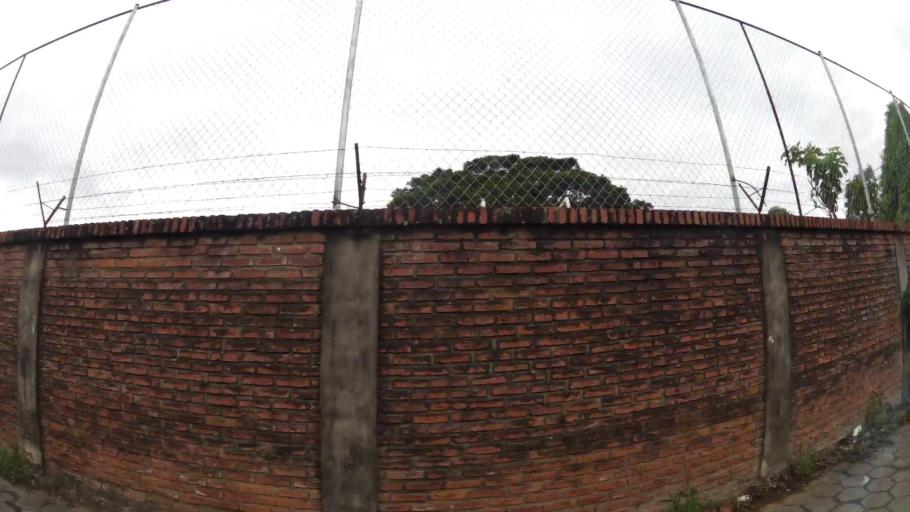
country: BO
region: Santa Cruz
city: Santa Cruz de la Sierra
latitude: -17.7795
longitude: -63.1612
